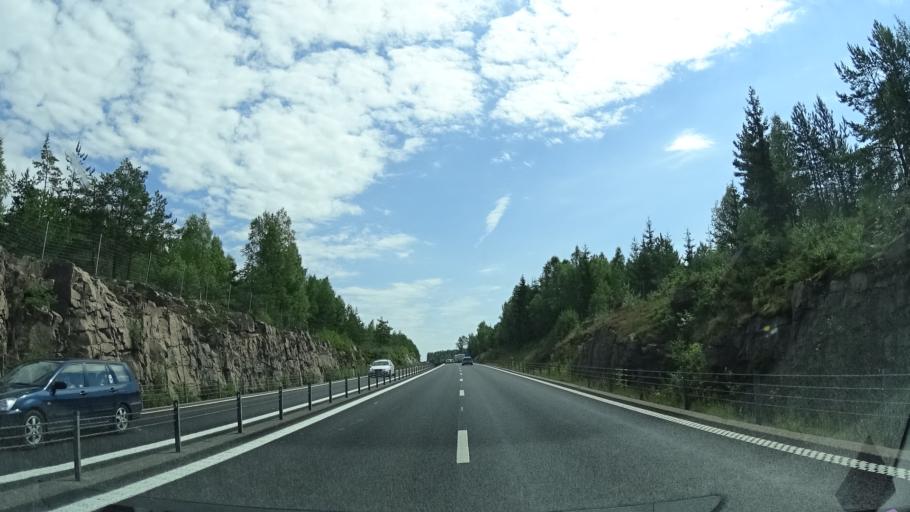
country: SE
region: Vaermland
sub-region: Karlstads Kommun
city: Skattkarr
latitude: 59.3930
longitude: 13.8257
